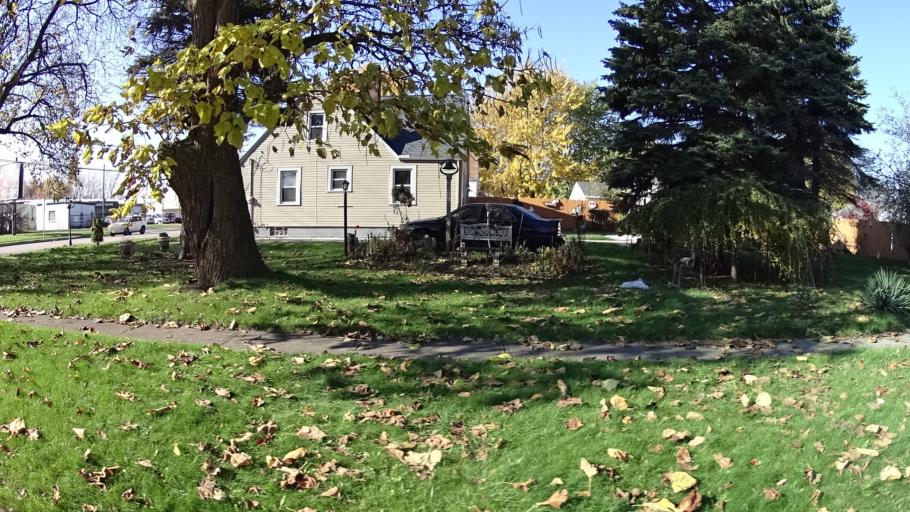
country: US
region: Ohio
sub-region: Lorain County
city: Lorain
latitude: 41.4657
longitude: -82.1537
